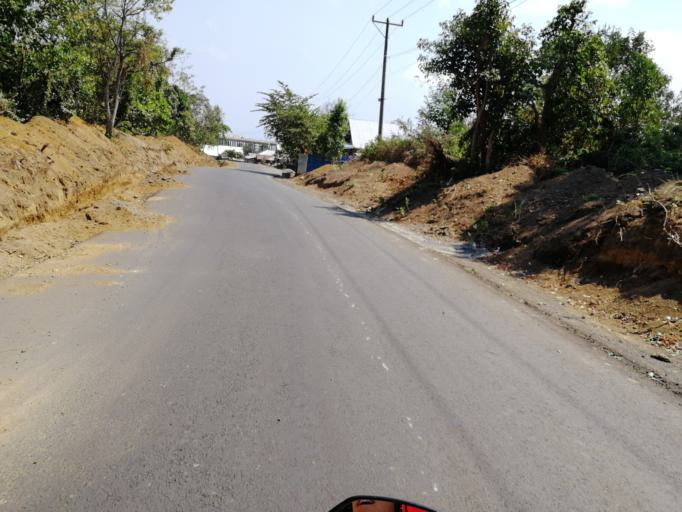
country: ID
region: West Nusa Tenggara
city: Lelongken
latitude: -8.3243
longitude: 116.4961
